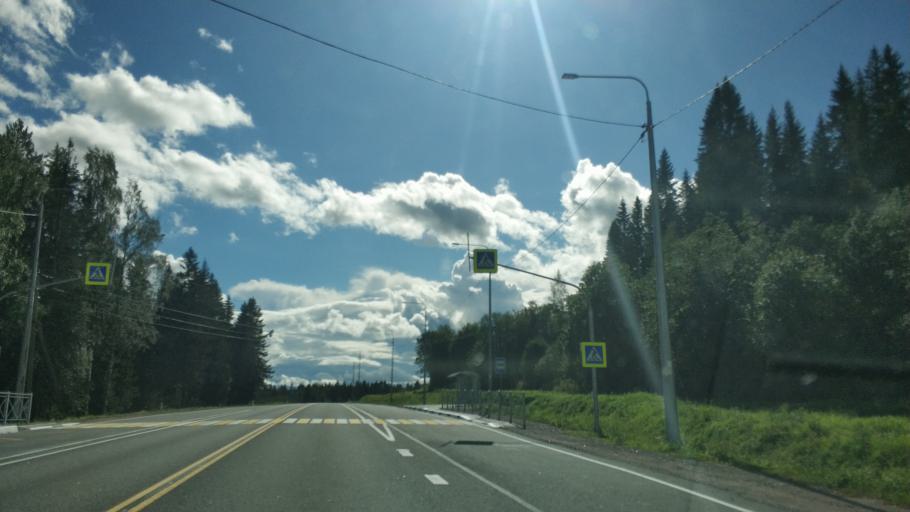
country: RU
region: Republic of Karelia
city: Ruskeala
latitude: 61.8848
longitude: 30.6440
